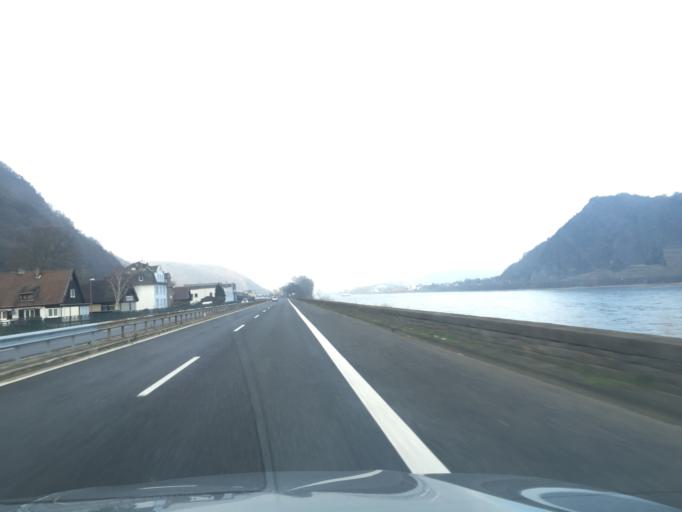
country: DE
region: Rheinland-Pfalz
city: Hammerstein
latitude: 50.4758
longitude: 7.3418
